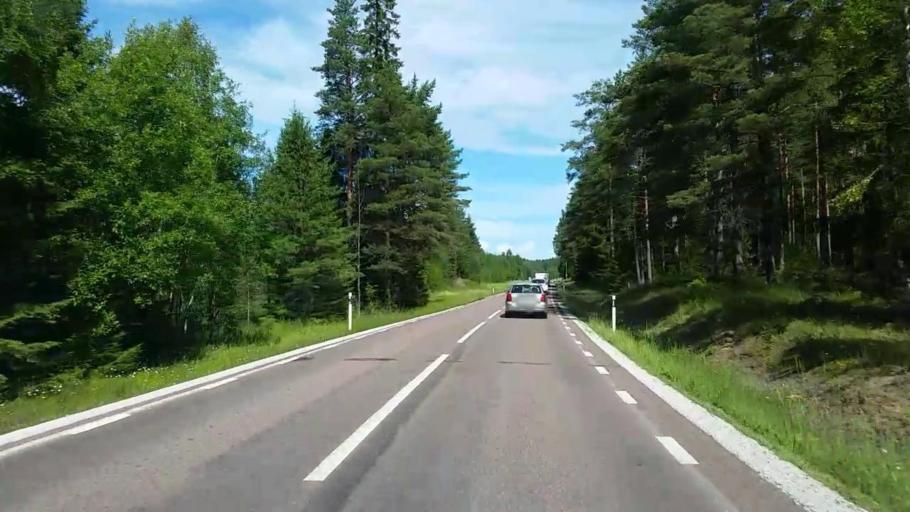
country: SE
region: Dalarna
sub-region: Rattviks Kommun
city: Raettvik
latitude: 60.9165
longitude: 15.2038
